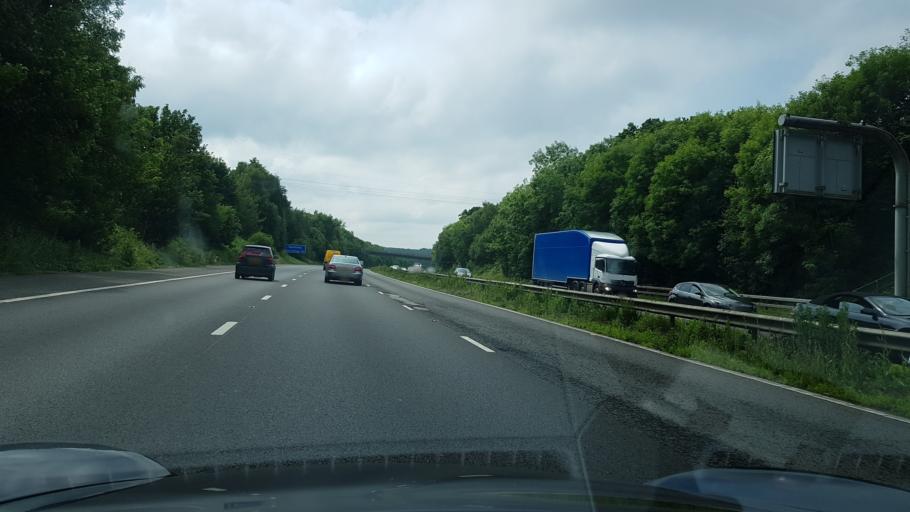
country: GB
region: England
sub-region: West Sussex
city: Maidenbower
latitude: 51.1153
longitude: -0.1372
